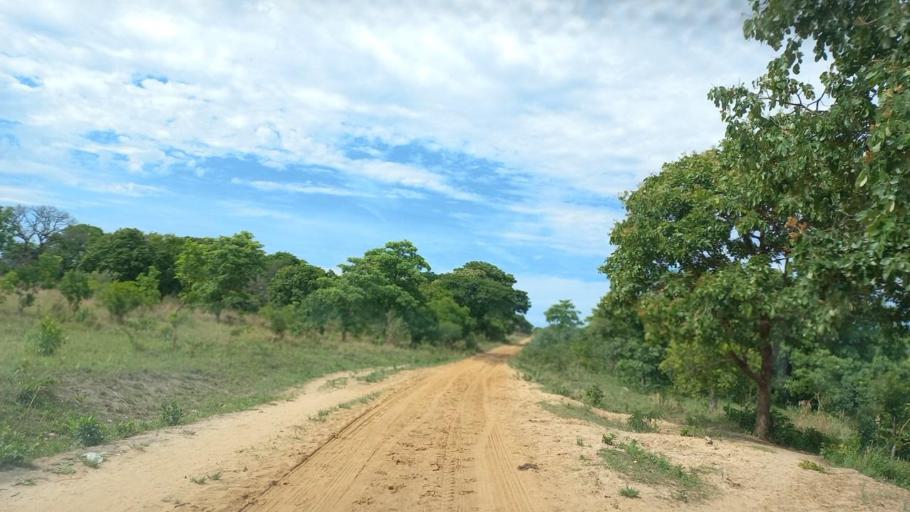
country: ZM
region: North-Western
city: Kabompo
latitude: -13.5103
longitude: 24.3942
